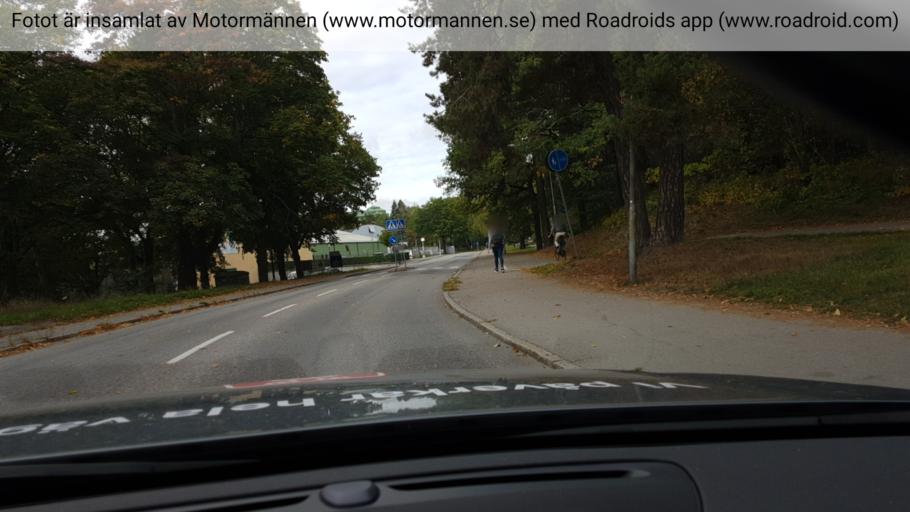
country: SE
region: Stockholm
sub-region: Stockholms Kommun
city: OEstermalm
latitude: 59.3510
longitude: 18.0838
